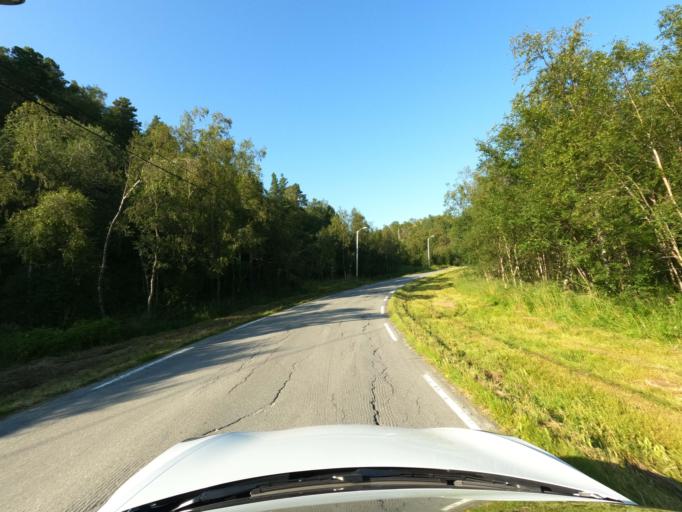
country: NO
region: Nordland
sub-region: Narvik
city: Bjerkvik
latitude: 68.4747
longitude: 17.5090
